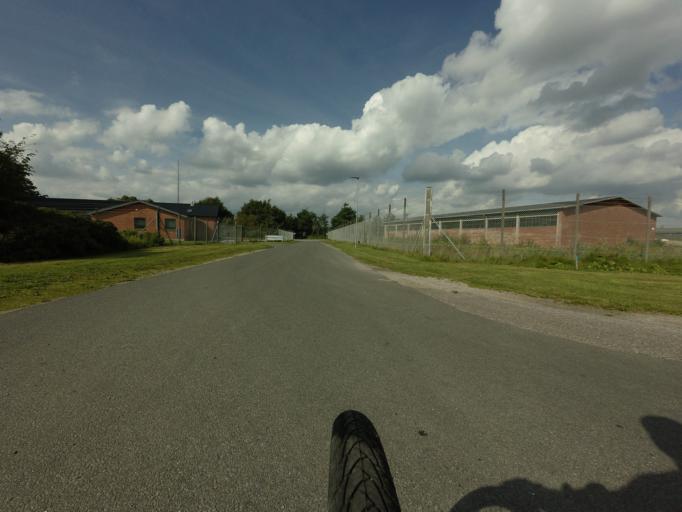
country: DK
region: Central Jutland
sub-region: Viborg Kommune
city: Karup
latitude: 56.2774
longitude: 9.1206
